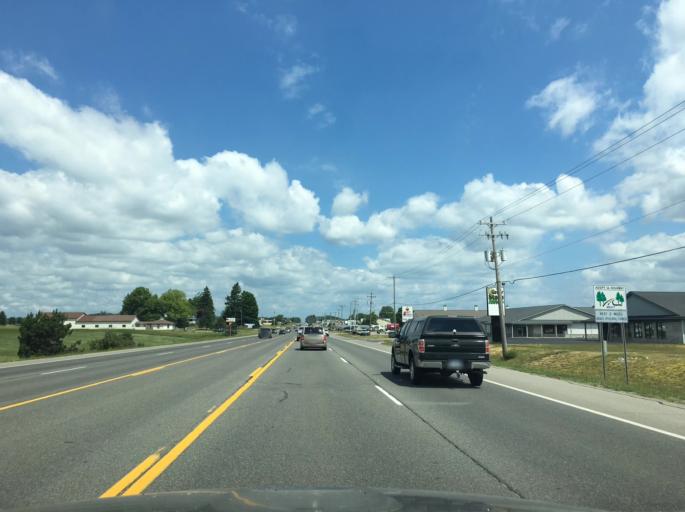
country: US
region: Michigan
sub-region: Grand Traverse County
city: Traverse City
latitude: 44.6871
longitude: -85.6562
